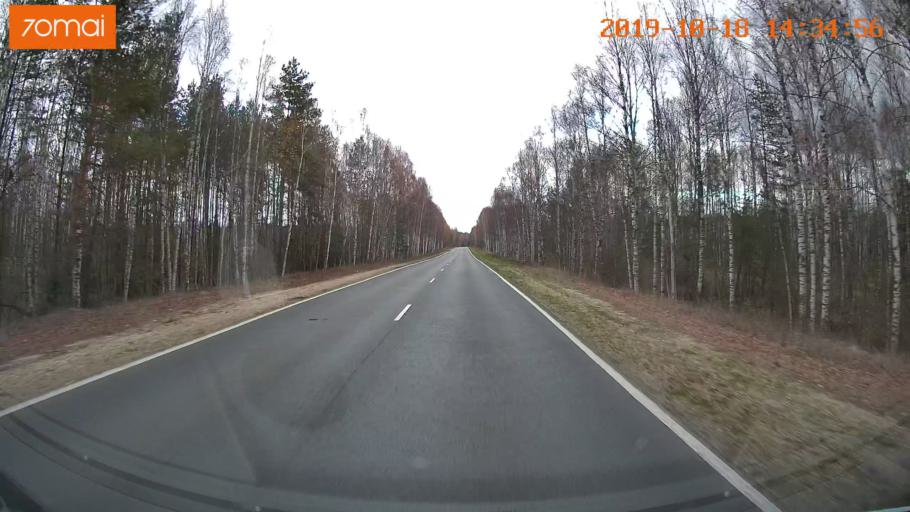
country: RU
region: Vladimir
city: Velikodvorskiy
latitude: 55.2177
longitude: 40.6261
